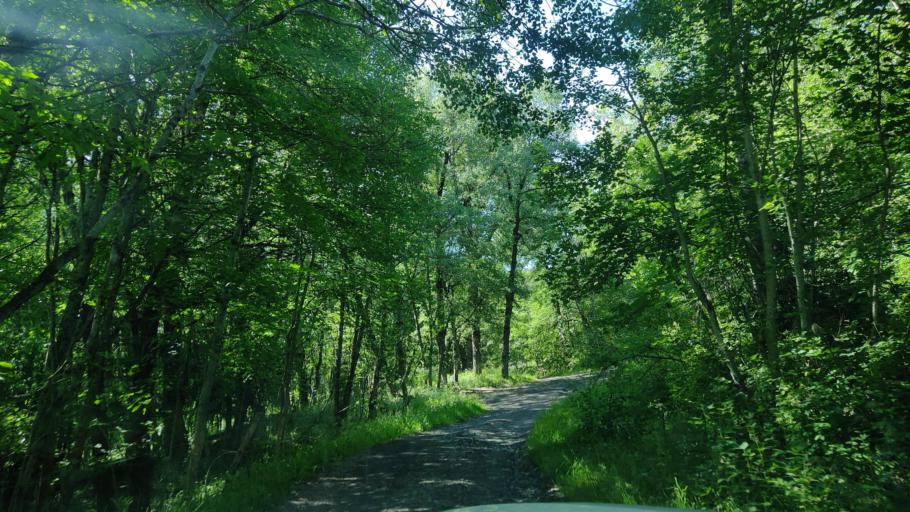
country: FR
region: Rhone-Alpes
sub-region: Departement de la Savoie
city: Saint-Jean-de-Maurienne
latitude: 45.2328
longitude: 6.2757
